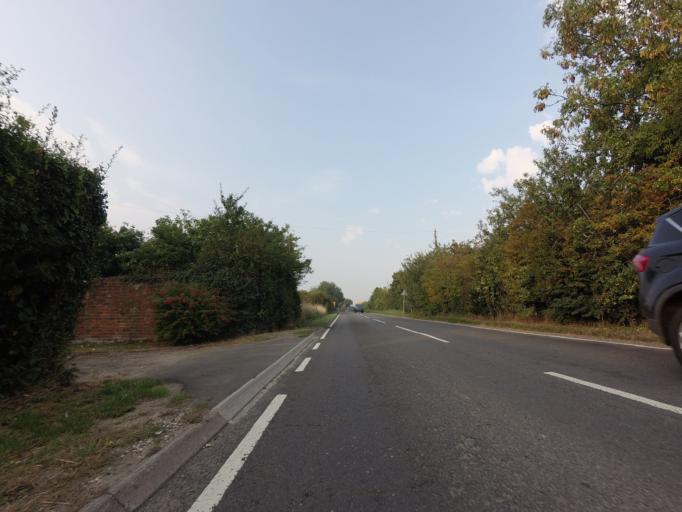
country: GB
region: England
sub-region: Kent
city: Ashford
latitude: 51.1346
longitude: 0.8189
